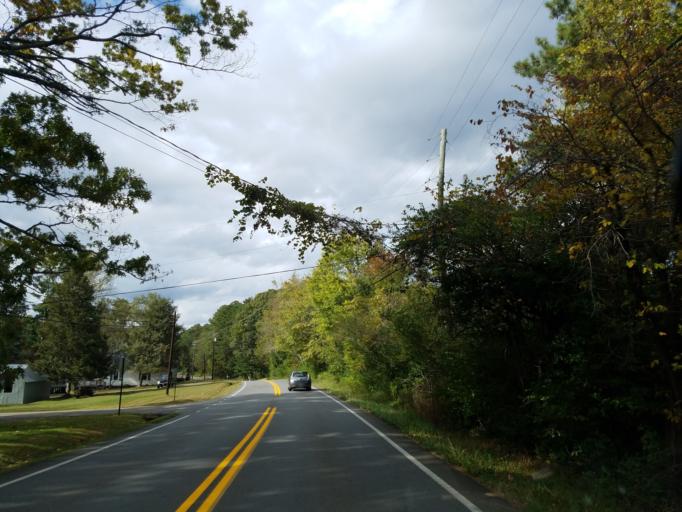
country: US
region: Georgia
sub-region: Pickens County
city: Jasper
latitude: 34.4531
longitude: -84.4247
